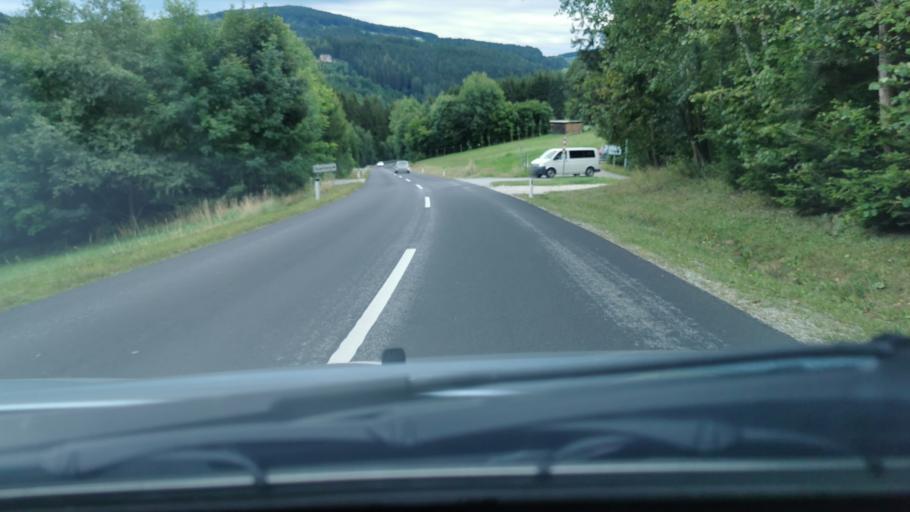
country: AT
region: Styria
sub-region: Politischer Bezirk Weiz
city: Birkfeld
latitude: 47.3626
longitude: 15.6888
